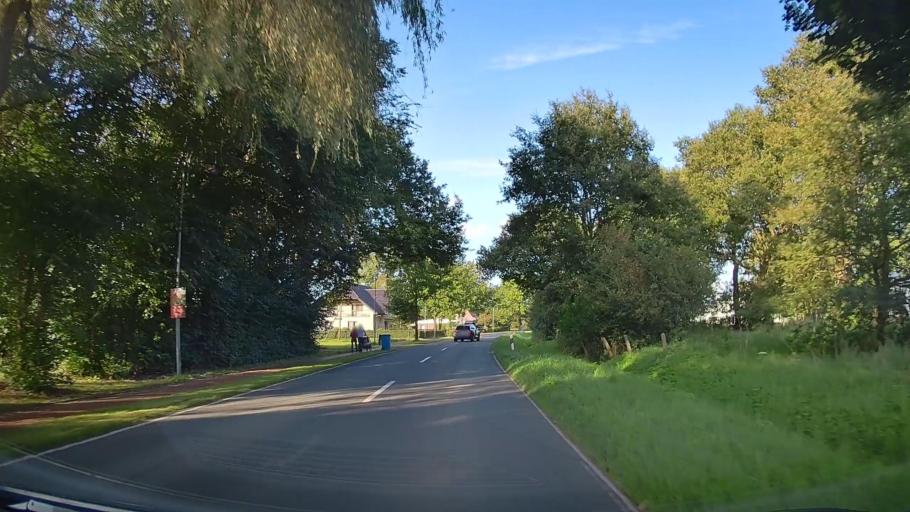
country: DE
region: Lower Saxony
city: Ostrhauderfehn
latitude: 53.1293
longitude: 7.6778
